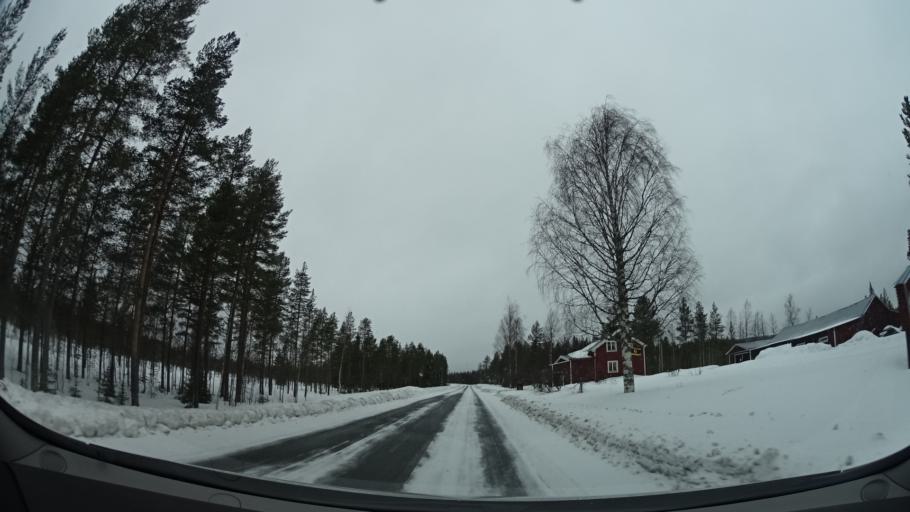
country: SE
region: Vaesterbotten
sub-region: Mala Kommun
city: Mala
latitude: 65.0814
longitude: 18.9999
